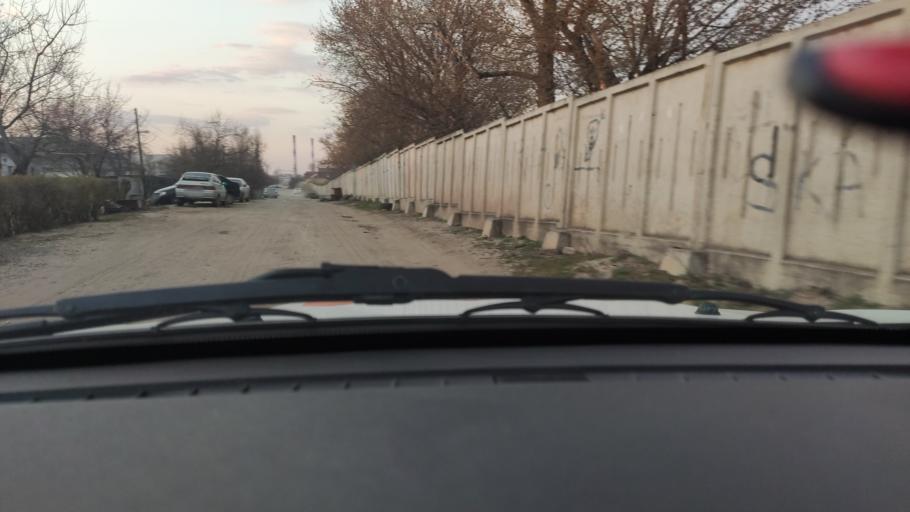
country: RU
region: Voronezj
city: Maslovka
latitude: 51.6066
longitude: 39.2247
